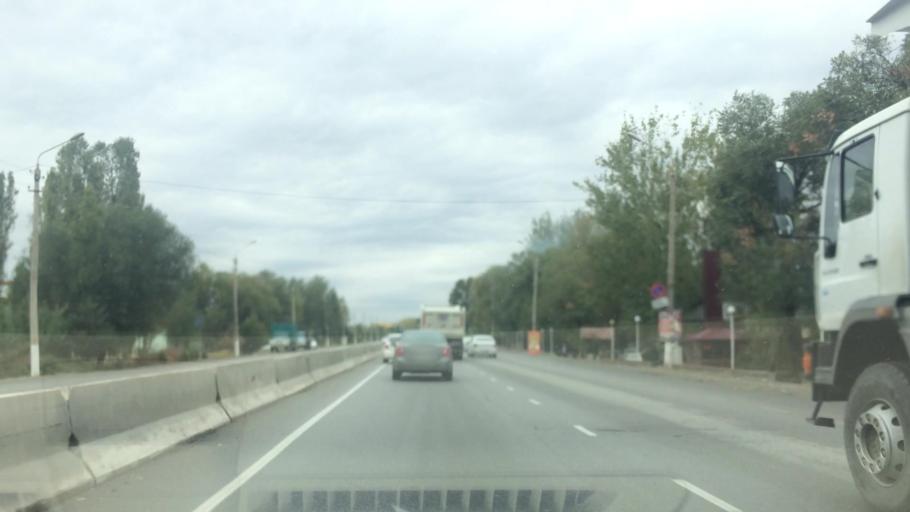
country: UZ
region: Jizzax
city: Jizzax
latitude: 39.9942
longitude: 67.5856
